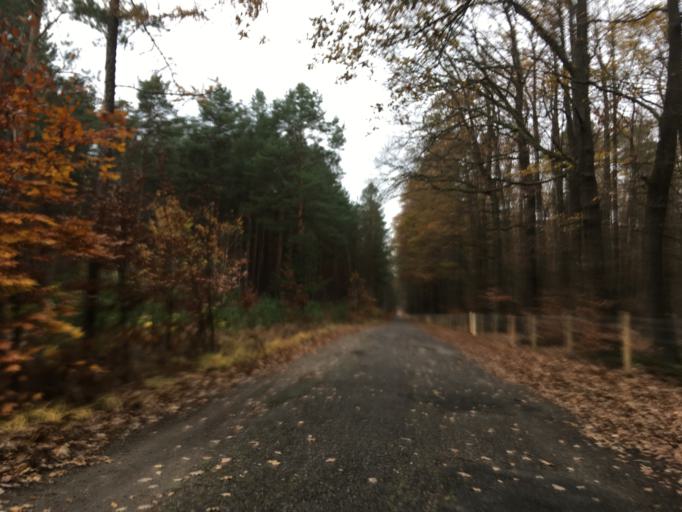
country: DE
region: Brandenburg
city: Jamlitz
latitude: 52.0731
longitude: 14.4805
